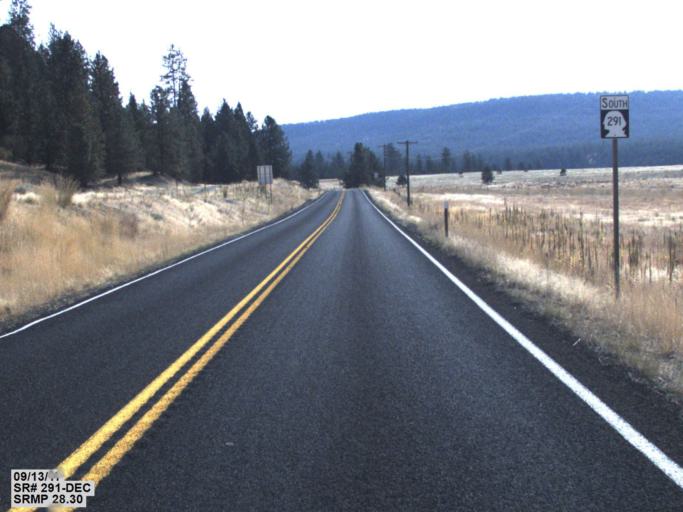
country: US
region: Washington
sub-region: Spokane County
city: Fairchild Air Force Base
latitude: 47.8382
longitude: -117.7590
